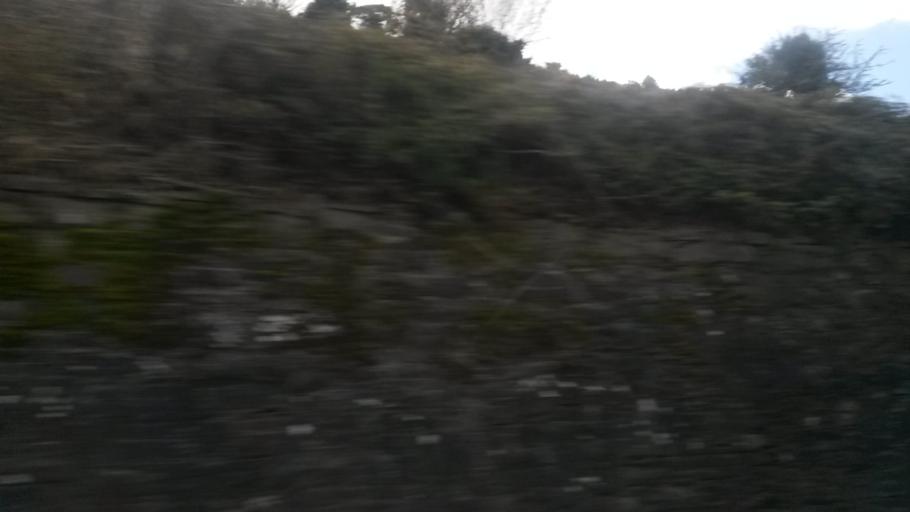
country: IE
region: Munster
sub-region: County Cork
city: Passage West
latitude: 51.8652
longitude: -8.3256
